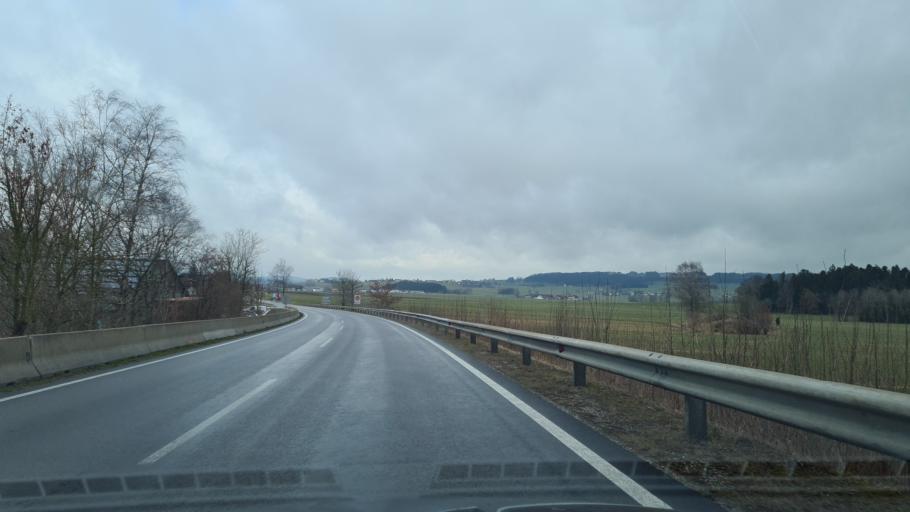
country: AT
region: Upper Austria
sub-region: Politischer Bezirk Vocklabruck
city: Oberhofen am Irrsee
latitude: 47.9613
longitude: 13.3018
